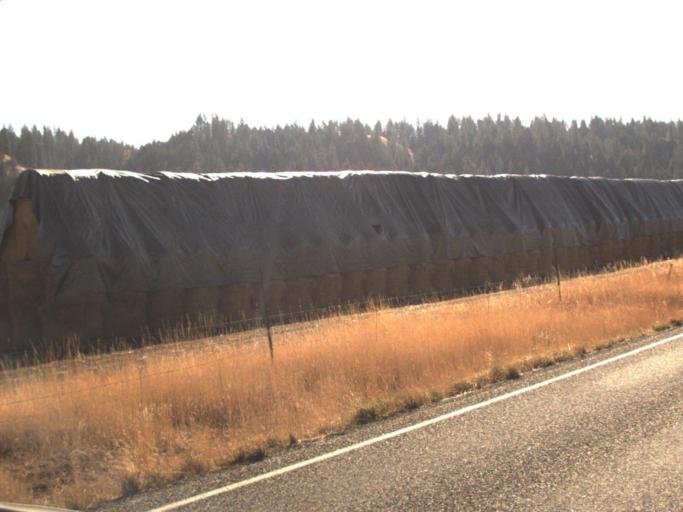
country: US
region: Washington
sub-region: Ferry County
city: Republic
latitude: 48.8119
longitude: -118.6004
